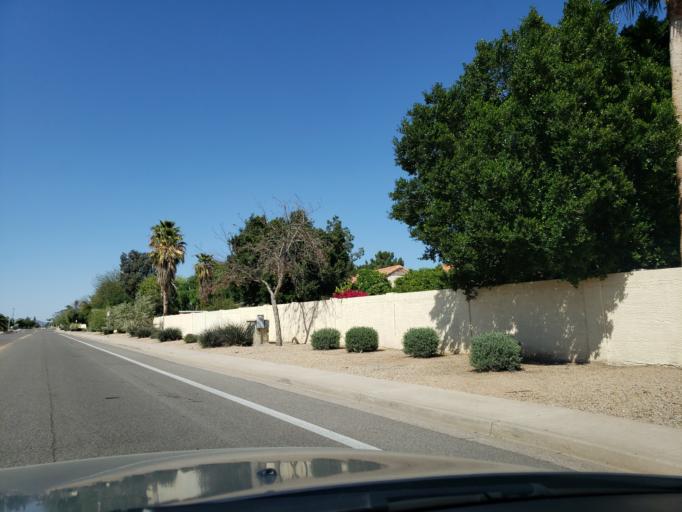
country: US
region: Arizona
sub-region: Maricopa County
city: Glendale
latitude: 33.5785
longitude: -112.1775
